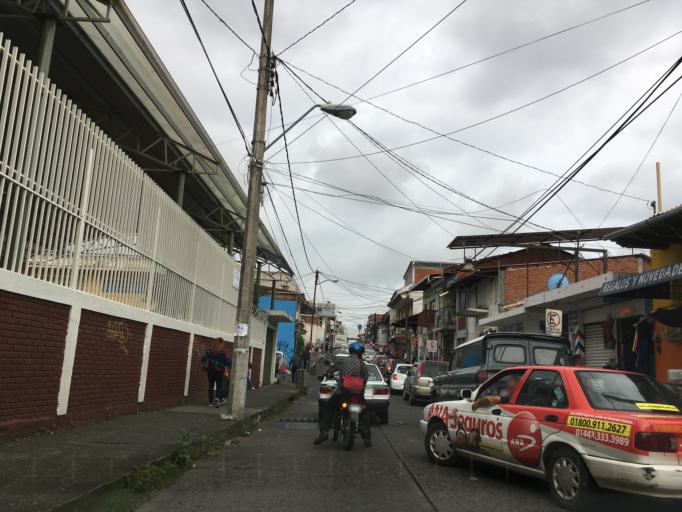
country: MX
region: Michoacan
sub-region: Uruapan
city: Uruapan
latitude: 19.4196
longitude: -102.0589
